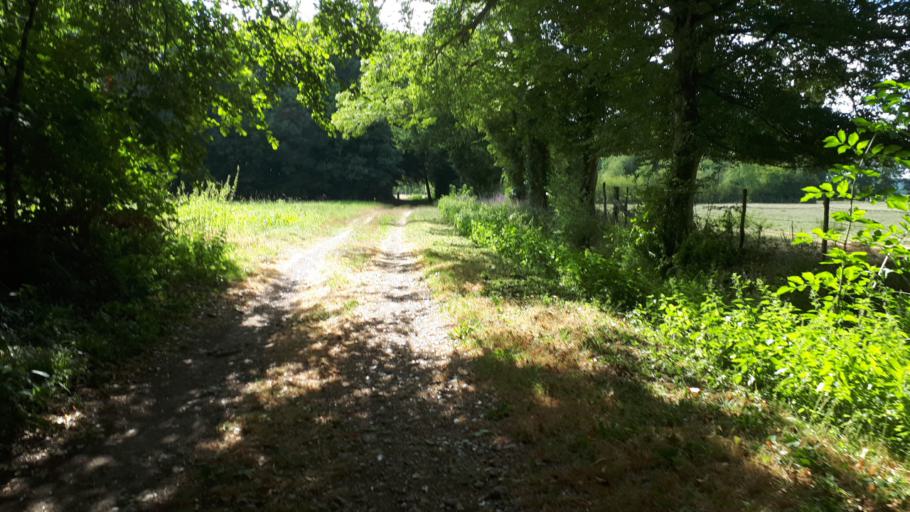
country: FR
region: Centre
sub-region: Departement du Loir-et-Cher
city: Villiers-sur-Loir
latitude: 47.7960
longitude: 0.9850
